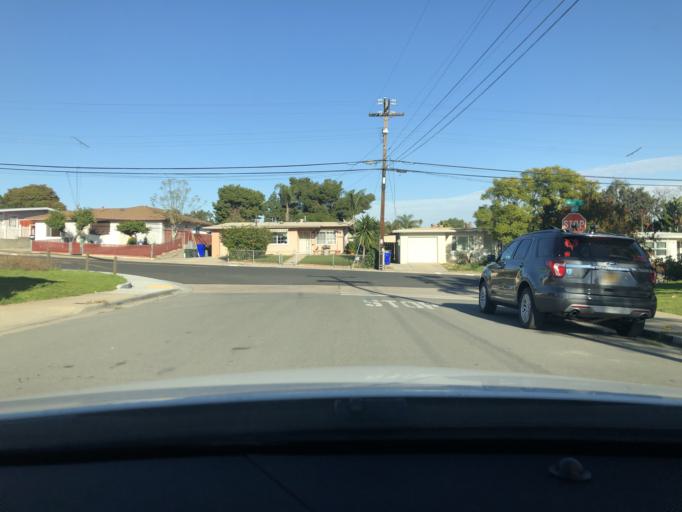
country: US
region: California
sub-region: San Diego County
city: Lemon Grove
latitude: 32.7464
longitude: -117.0629
